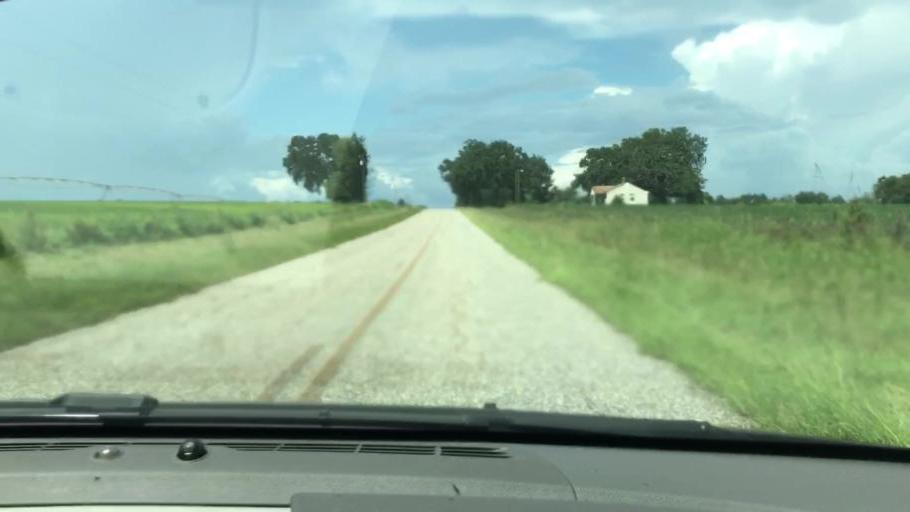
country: US
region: Georgia
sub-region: Seminole County
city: Donalsonville
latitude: 31.1887
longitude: -85.0042
